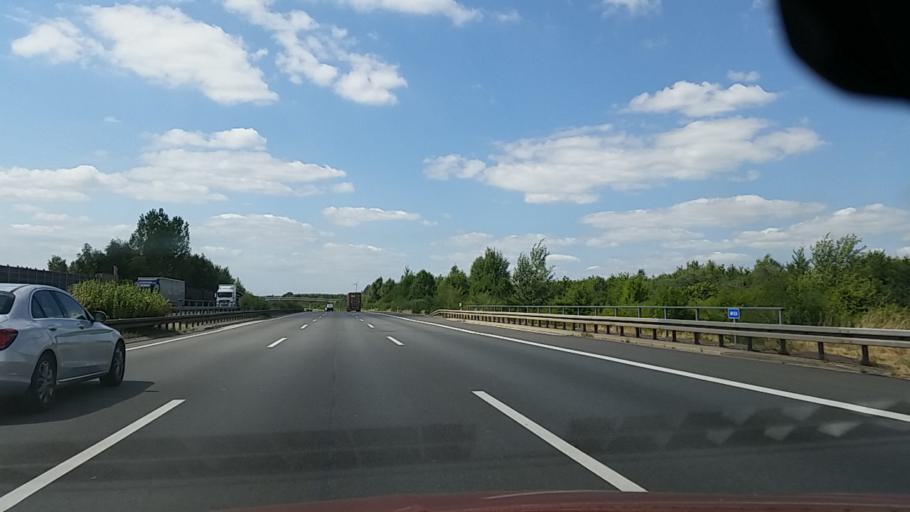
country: DE
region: Lower Saxony
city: Peine
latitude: 52.3530
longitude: 10.1952
